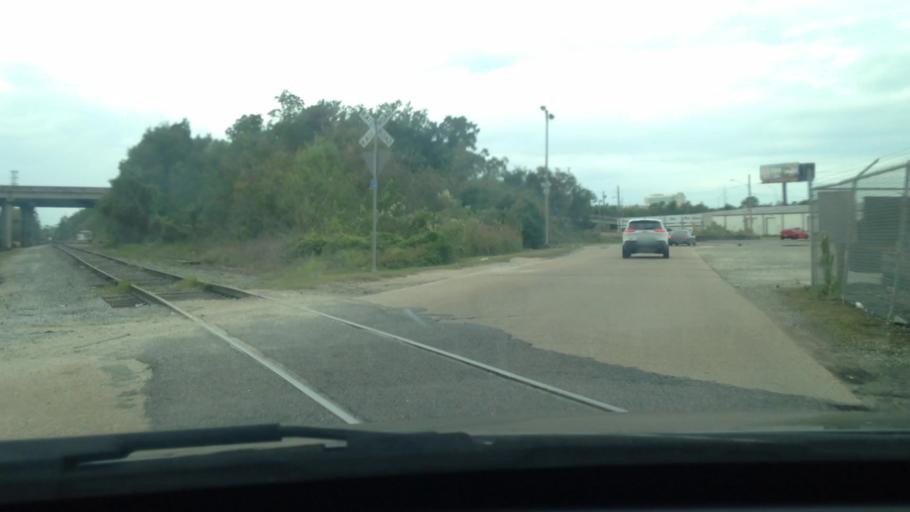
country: US
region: Louisiana
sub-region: Jefferson Parish
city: Jefferson
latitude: 29.9709
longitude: -90.1318
